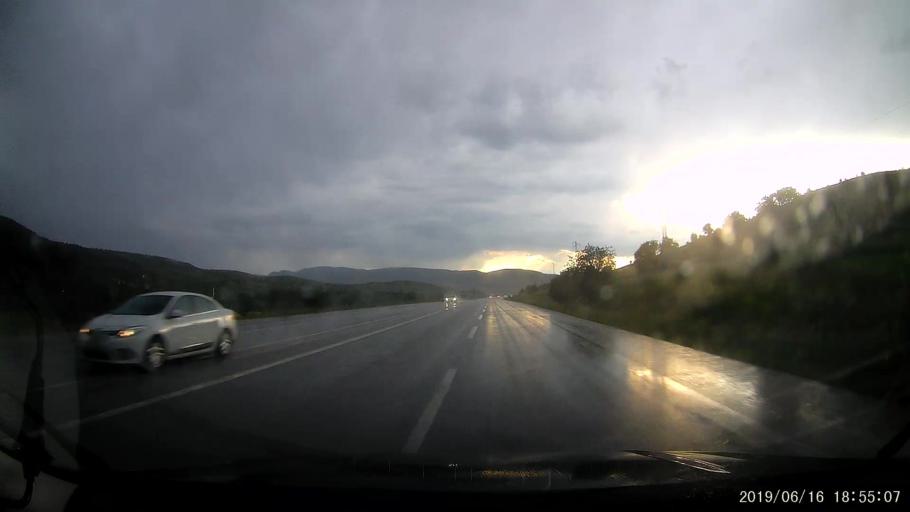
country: TR
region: Erzincan
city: Refahiye
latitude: 39.8989
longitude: 38.8362
